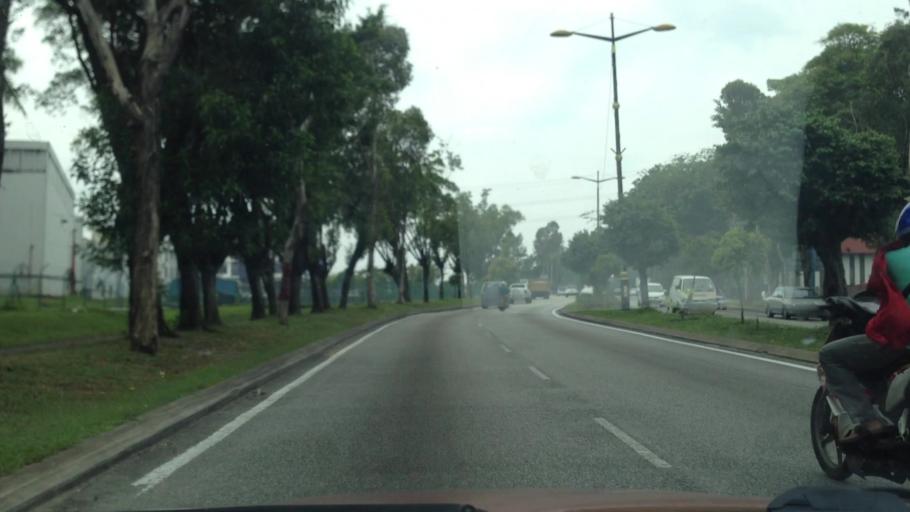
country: MY
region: Selangor
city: Shah Alam
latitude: 3.0640
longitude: 101.5408
